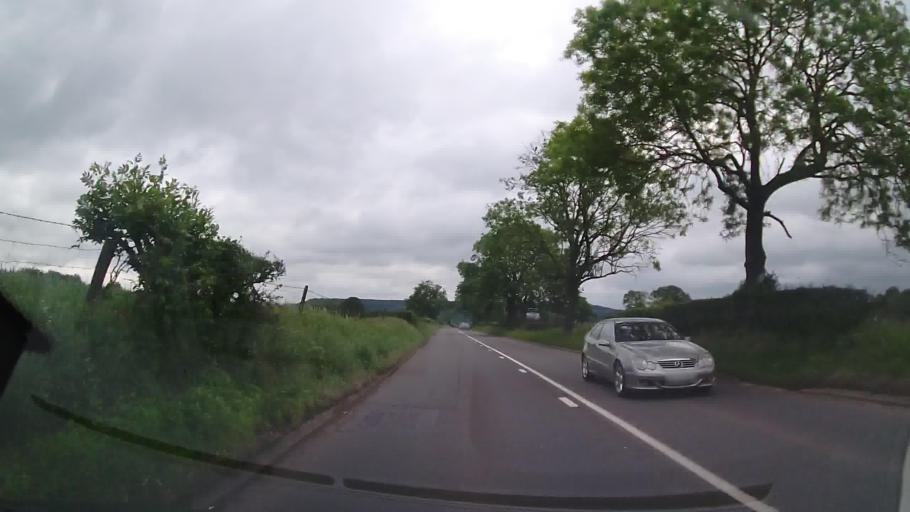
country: GB
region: England
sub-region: Staffordshire
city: Standon
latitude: 52.9334
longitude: -2.3589
